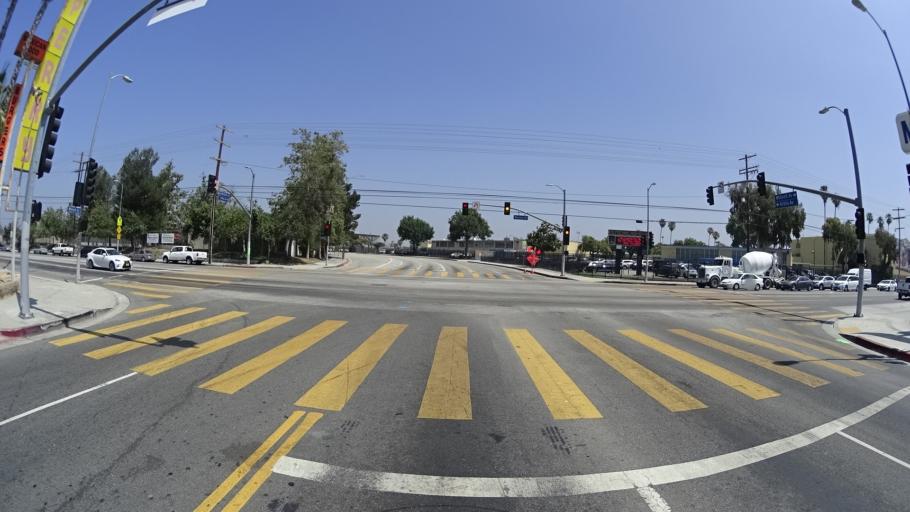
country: US
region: California
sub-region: Los Angeles County
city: North Hollywood
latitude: 34.2215
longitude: -118.4052
